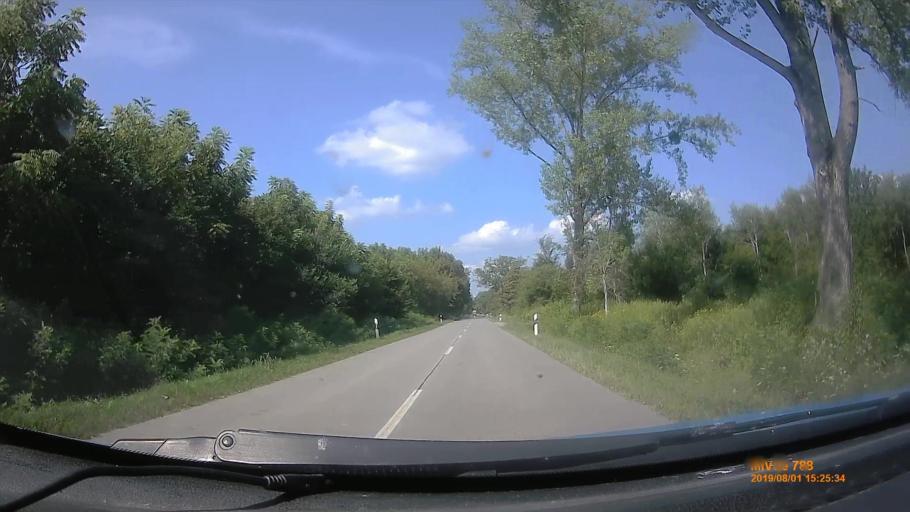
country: HU
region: Baranya
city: Sellye
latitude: 45.8949
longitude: 17.8551
